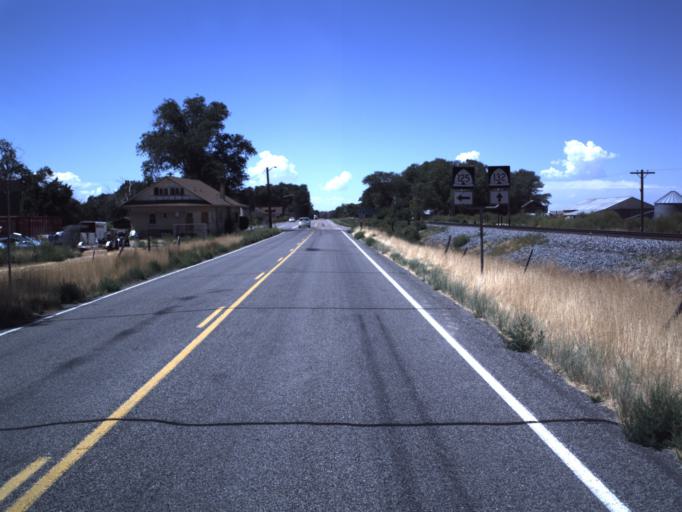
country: US
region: Utah
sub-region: Millard County
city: Delta
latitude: 39.5363
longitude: -112.2718
